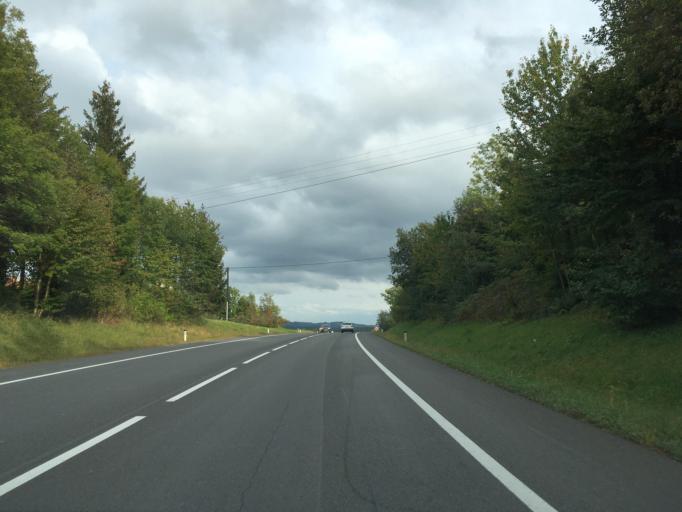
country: AT
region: Styria
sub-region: Politischer Bezirk Hartberg-Fuerstenfeld
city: Dechantskirchen
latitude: 47.4146
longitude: 16.0172
